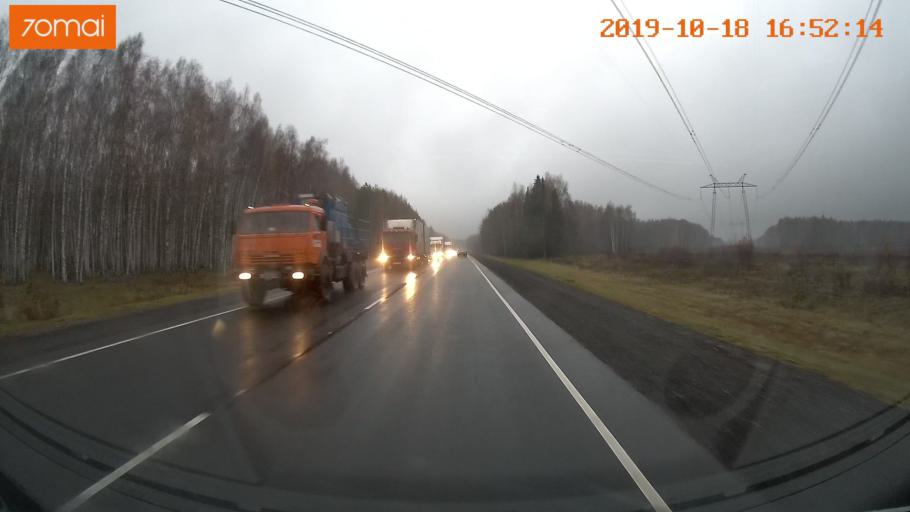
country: RU
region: Vladimir
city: Kideksha
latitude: 56.5976
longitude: 40.5558
